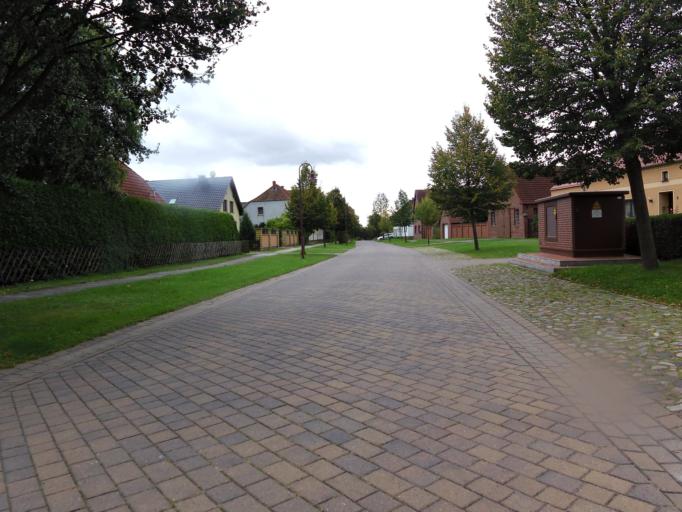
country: DE
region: Saxony-Anhalt
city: Tangermunde
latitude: 52.5903
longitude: 11.9870
